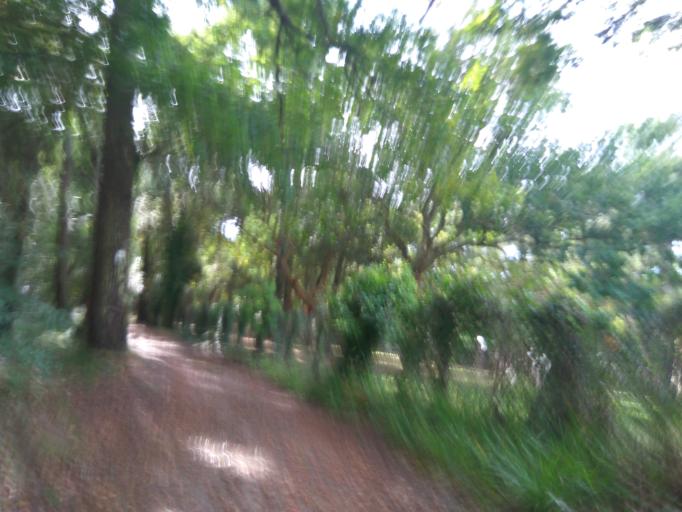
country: FR
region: Aquitaine
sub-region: Departement des Landes
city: Capbreton
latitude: 43.6290
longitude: -1.4440
